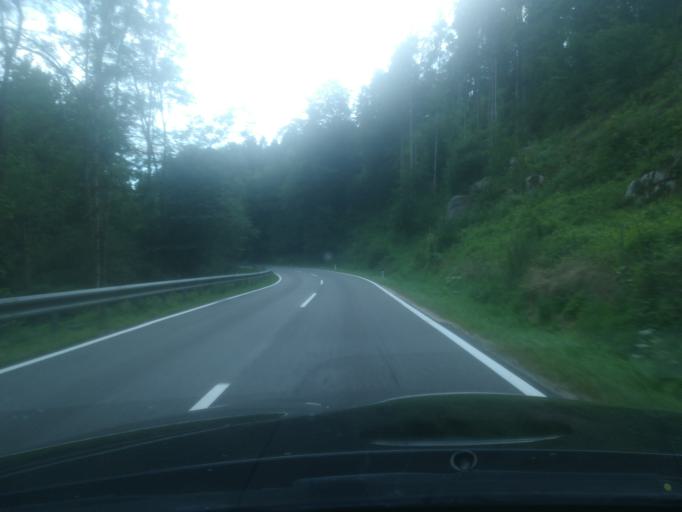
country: AT
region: Upper Austria
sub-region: Politischer Bezirk Perg
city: Perg
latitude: 48.3307
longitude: 14.5667
